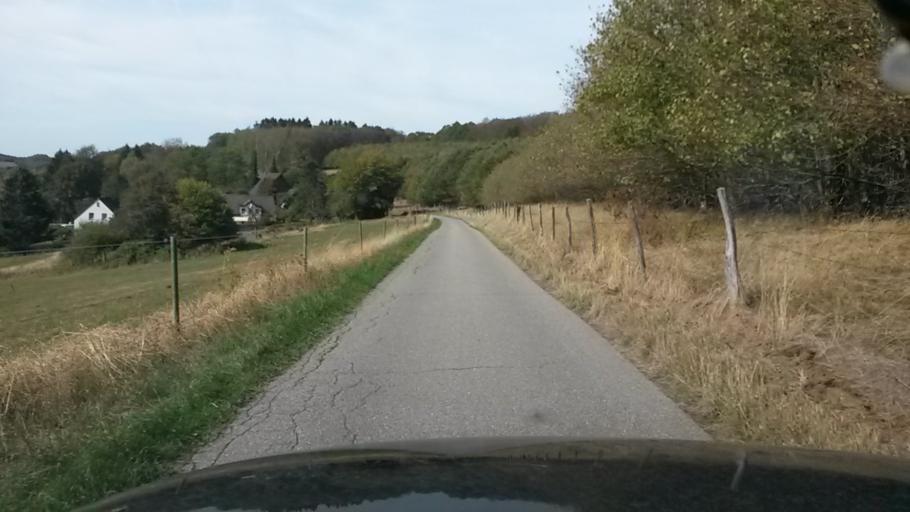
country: DE
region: North Rhine-Westphalia
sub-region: Regierungsbezirk Arnsberg
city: Herscheid
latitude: 51.1905
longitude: 7.7317
